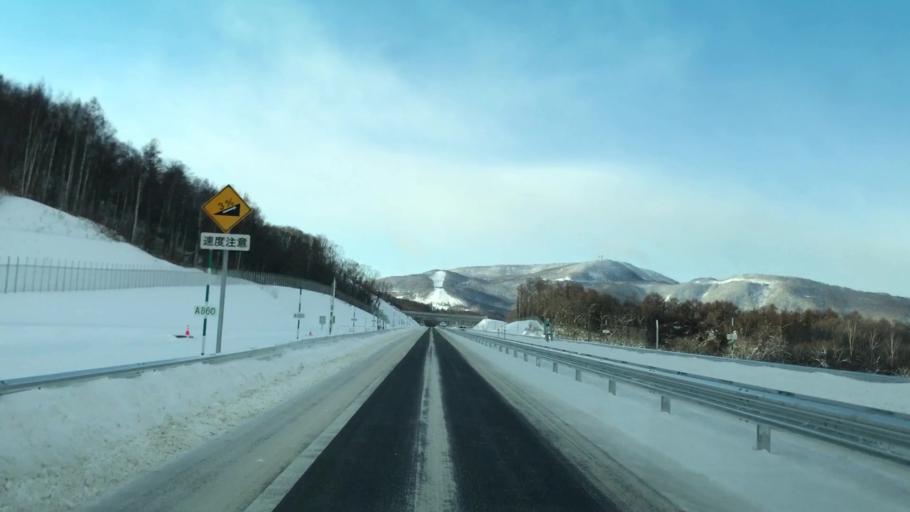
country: JP
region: Hokkaido
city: Otaru
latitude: 43.1673
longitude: 141.0637
